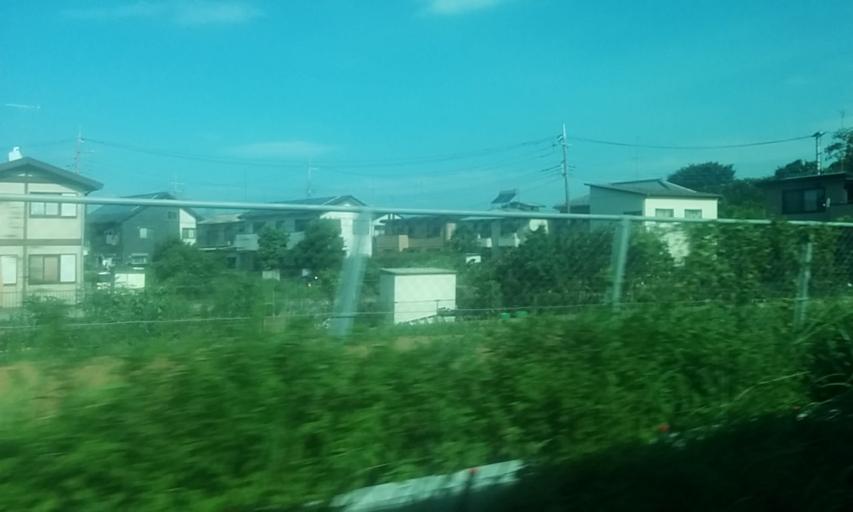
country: JP
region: Saitama
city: Shiraoka
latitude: 36.0021
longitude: 139.6642
